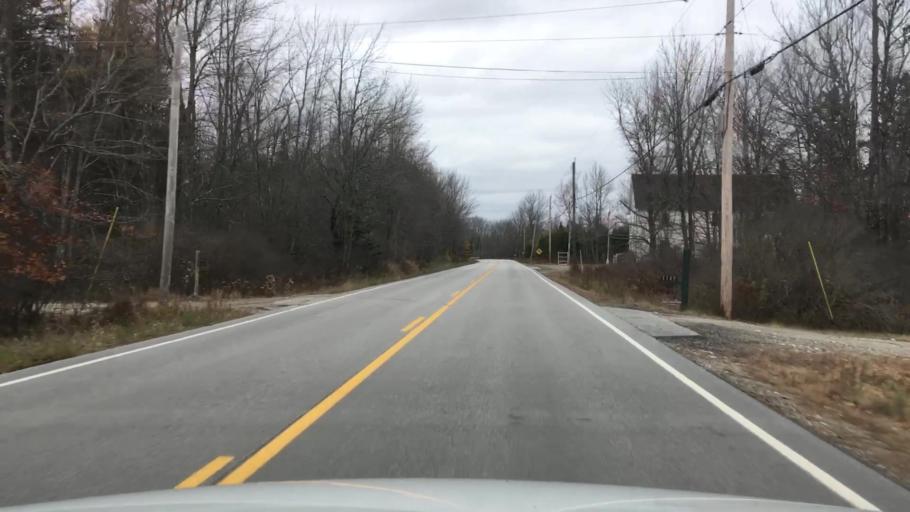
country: US
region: Maine
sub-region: Hancock County
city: Penobscot
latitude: 44.4658
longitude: -68.6365
